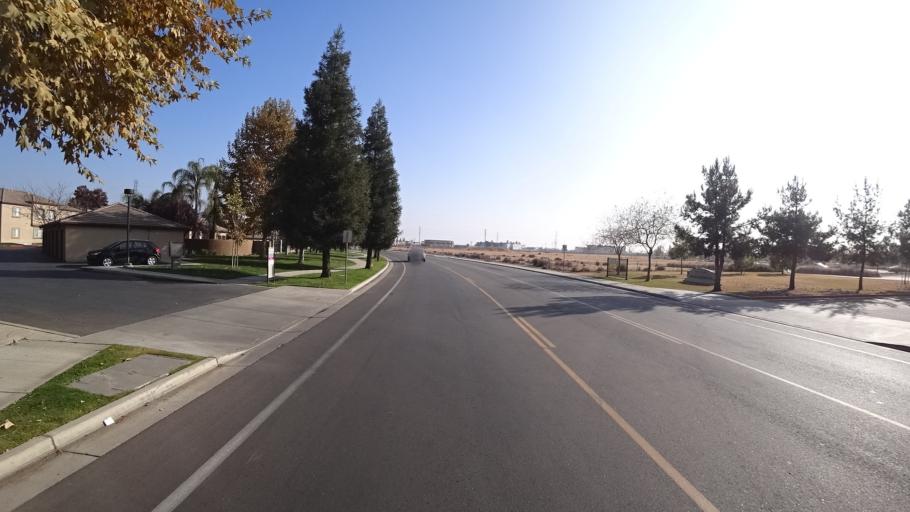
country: US
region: California
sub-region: Kern County
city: Greenacres
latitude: 35.3954
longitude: -119.0957
